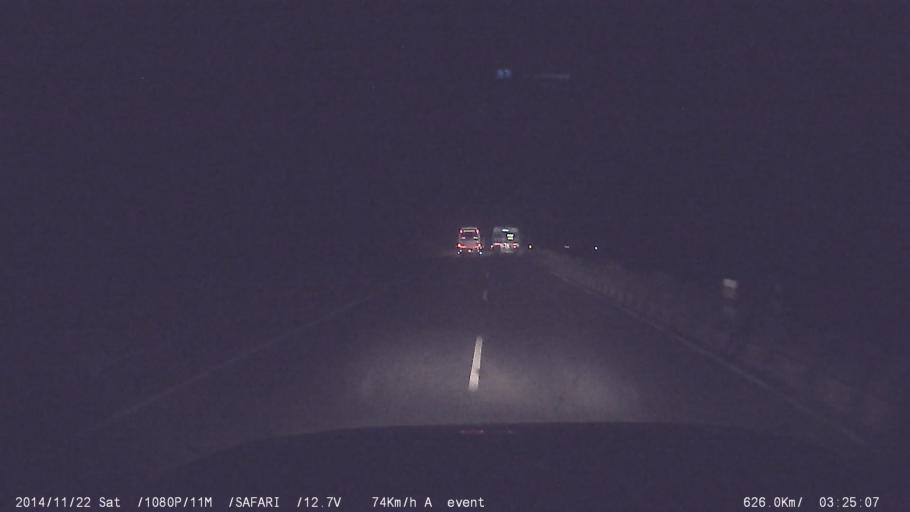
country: IN
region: Tamil Nadu
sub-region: Salem
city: Ilampillai
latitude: 11.5416
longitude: 77.9761
